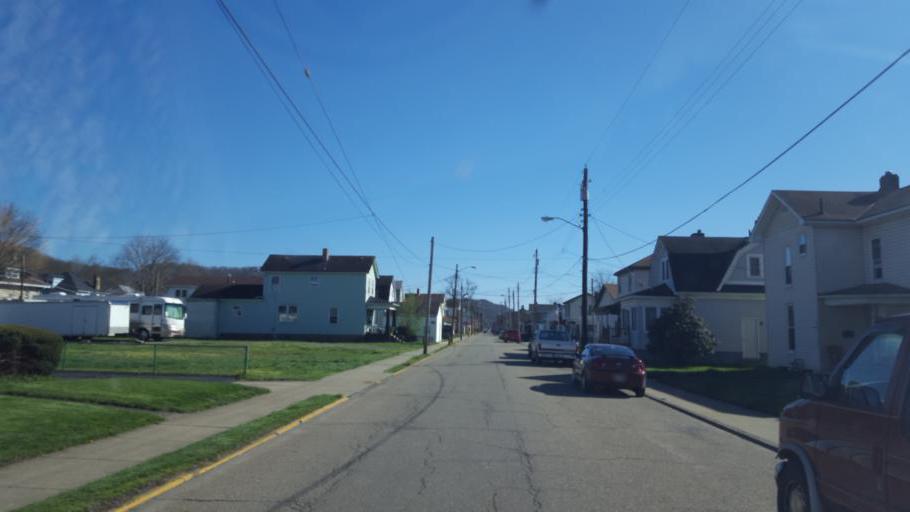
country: US
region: Ohio
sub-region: Jefferson County
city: Toronto
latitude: 40.4704
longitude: -80.6007
